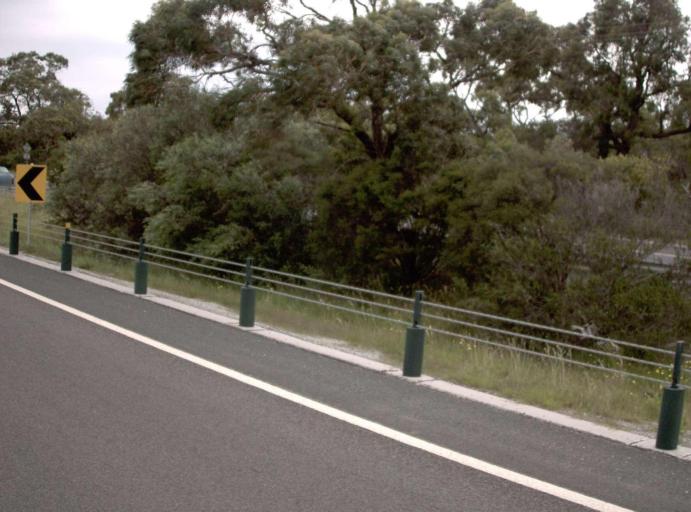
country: AU
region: Victoria
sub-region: Casey
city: Junction Village
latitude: -38.1275
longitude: 145.2906
